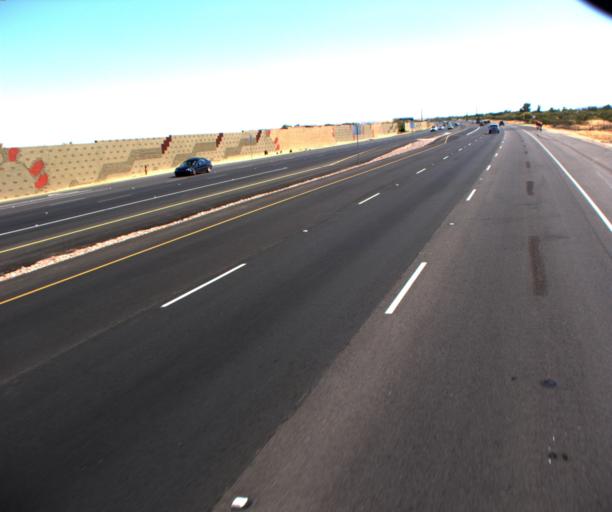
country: US
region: Arizona
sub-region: Pima County
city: Catalina
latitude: 32.4550
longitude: -110.9310
